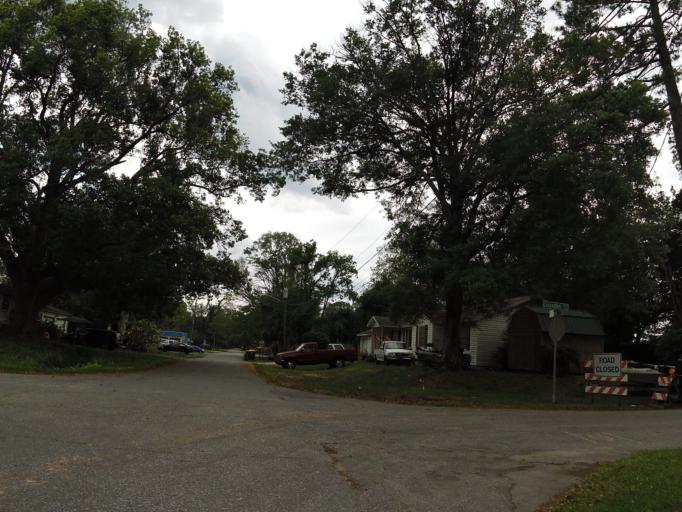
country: US
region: Florida
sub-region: Duval County
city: Jacksonville
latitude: 30.2832
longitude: -81.7283
